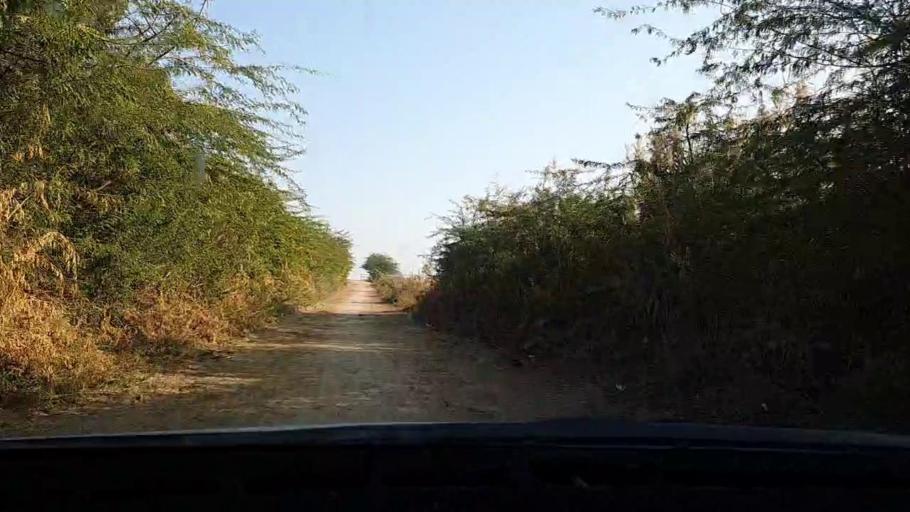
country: PK
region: Sindh
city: Tando Mittha Khan
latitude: 25.8330
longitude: 69.3198
